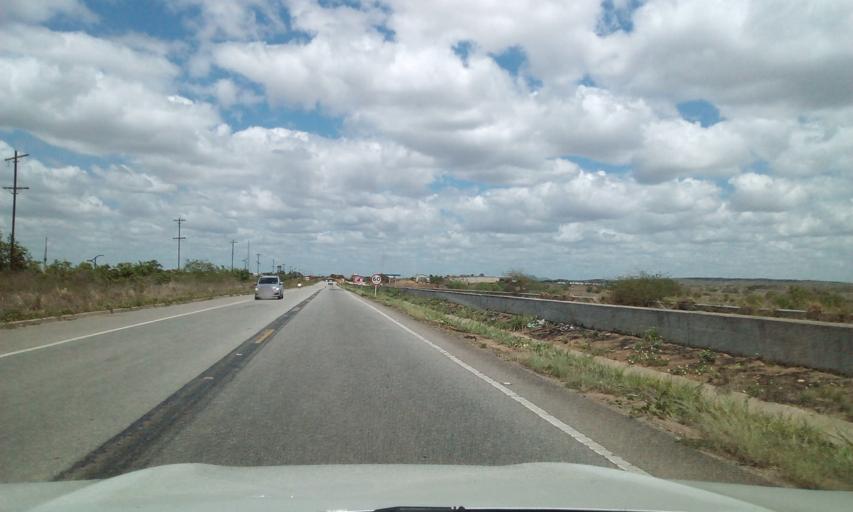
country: BR
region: Alagoas
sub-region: Porto Real Do Colegio
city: Porto Real do Colegio
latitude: -10.1921
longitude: -36.8251
